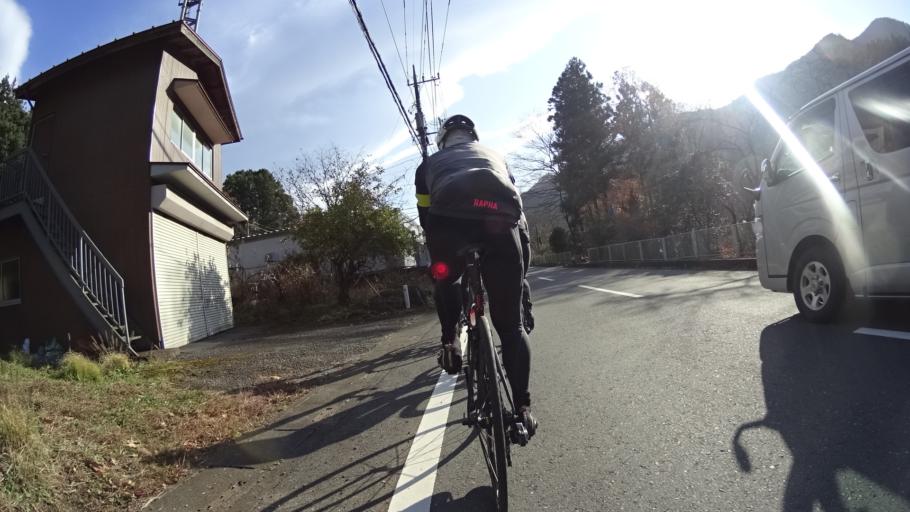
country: JP
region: Tokyo
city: Ome
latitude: 35.8945
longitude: 139.1772
